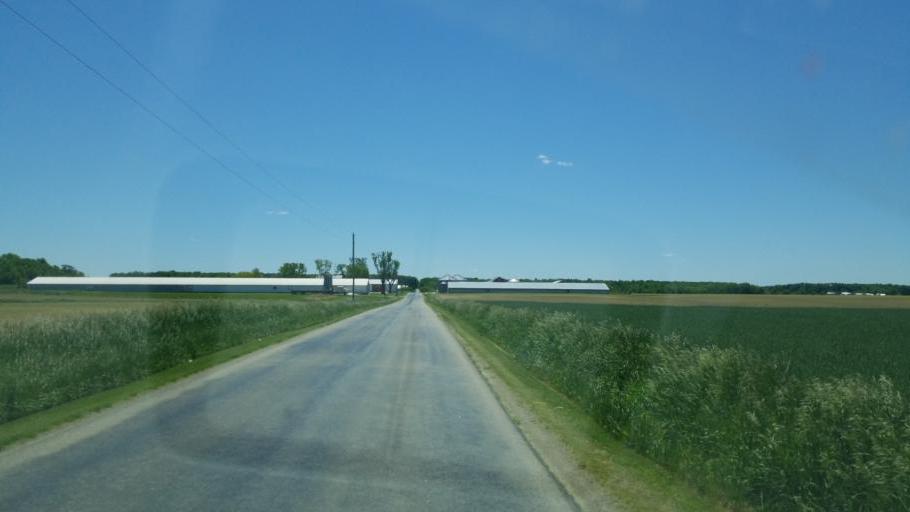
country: US
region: Ohio
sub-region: Mercer County
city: Fort Recovery
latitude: 40.3375
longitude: -84.8037
